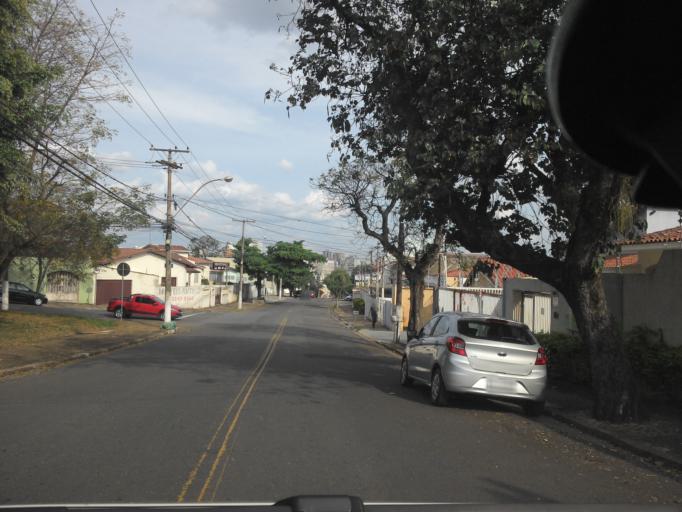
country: BR
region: Sao Paulo
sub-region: Campinas
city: Campinas
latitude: -22.8932
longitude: -47.0733
